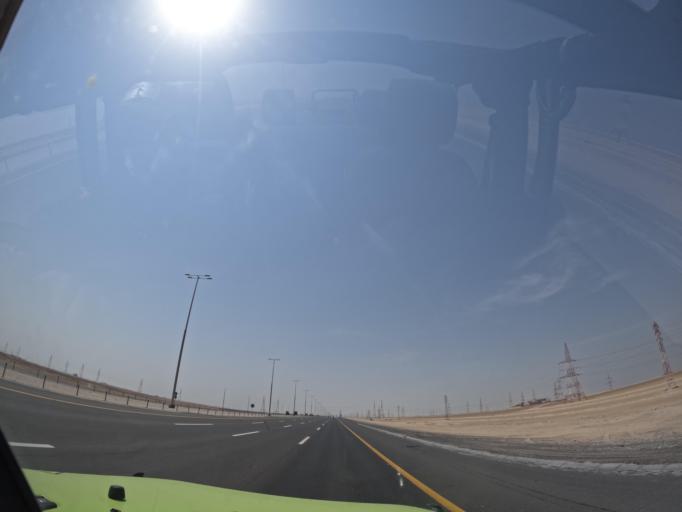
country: AE
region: Abu Dhabi
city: Abu Dhabi
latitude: 24.1564
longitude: 54.3141
